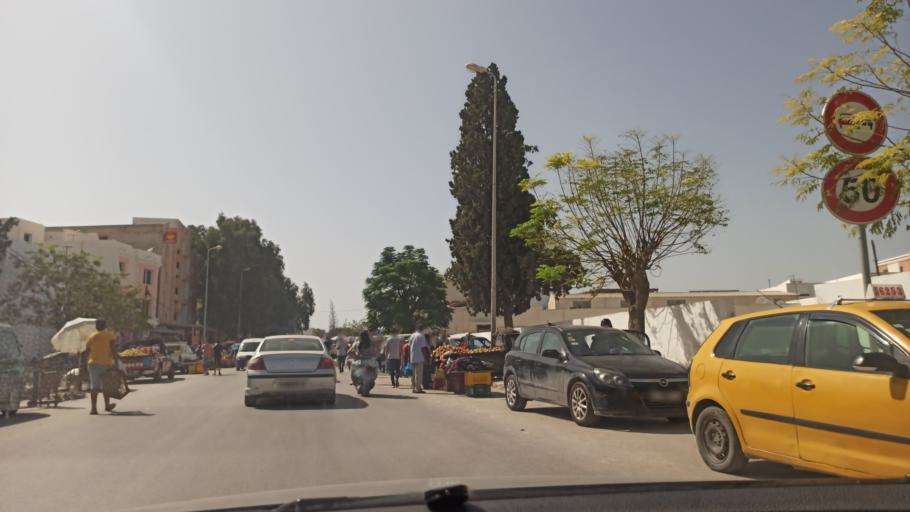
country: TN
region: Manouba
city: Manouba
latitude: 36.7674
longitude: 10.1115
